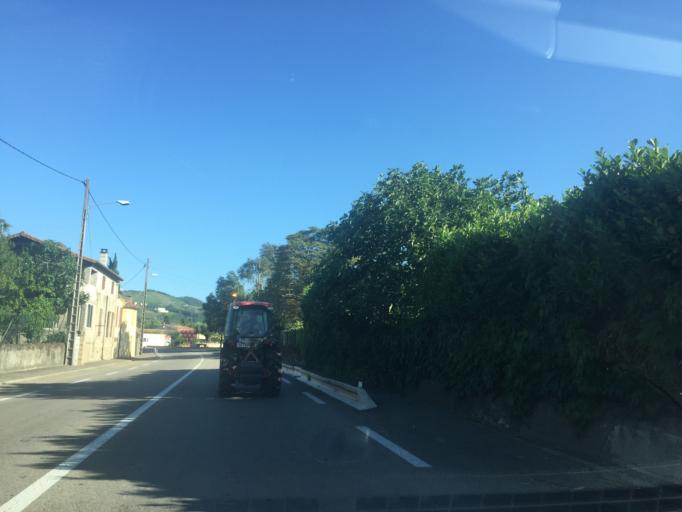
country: FR
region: Rhone-Alpes
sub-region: Departement de l'Ardeche
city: Tournon-sur-Rhone
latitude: 45.0634
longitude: 4.8583
